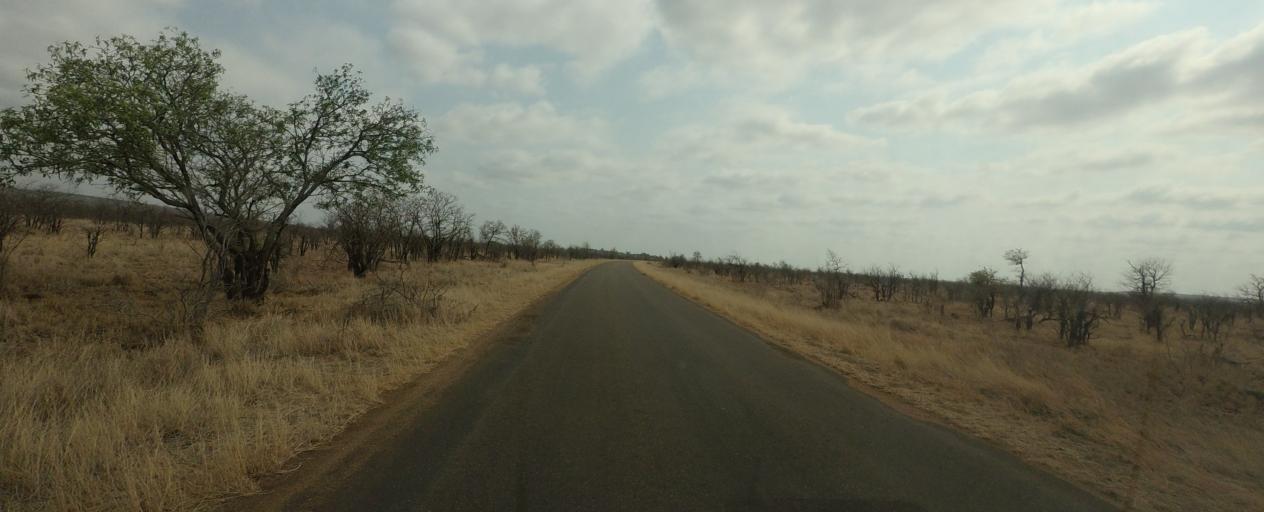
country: ZA
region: Limpopo
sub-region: Vhembe District Municipality
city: Mutale
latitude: -22.6104
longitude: 31.1738
